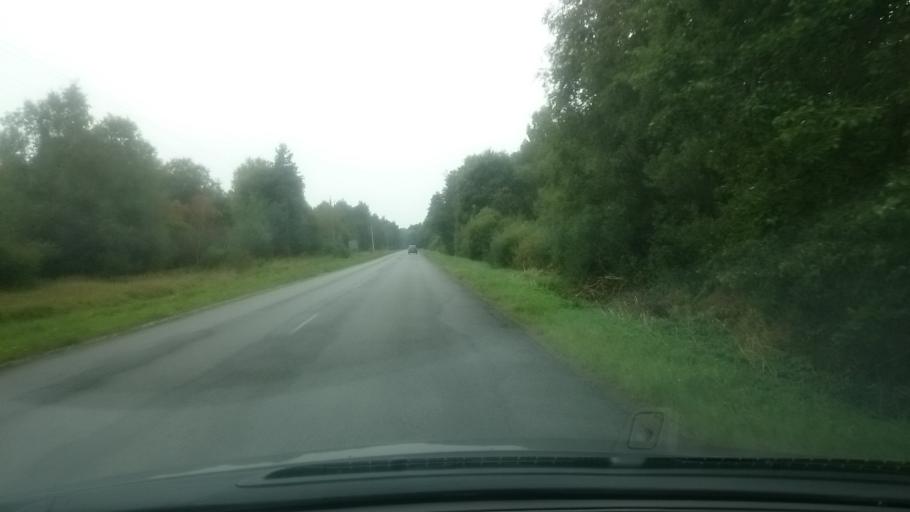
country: EE
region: Harju
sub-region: Raasiku vald
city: Raasiku
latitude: 59.4486
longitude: 25.1984
